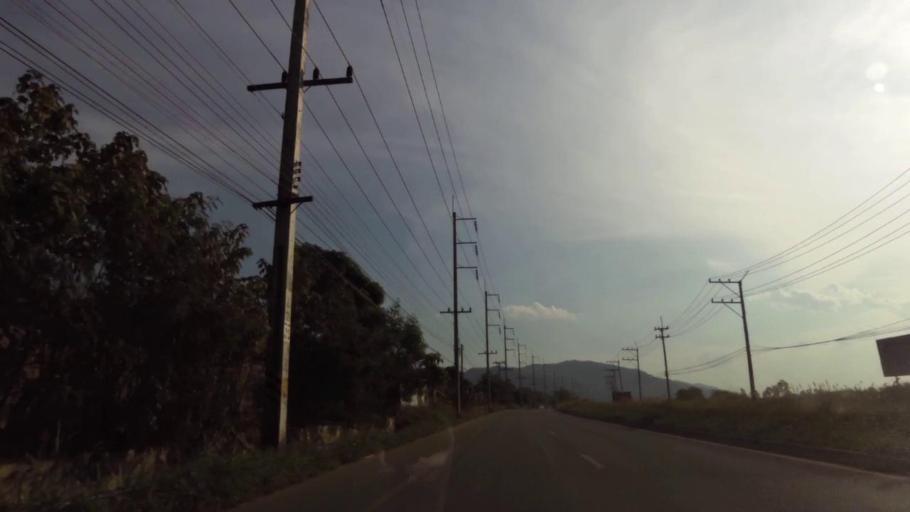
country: TH
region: Chiang Rai
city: Khun Tan
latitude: 19.8891
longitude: 100.2938
